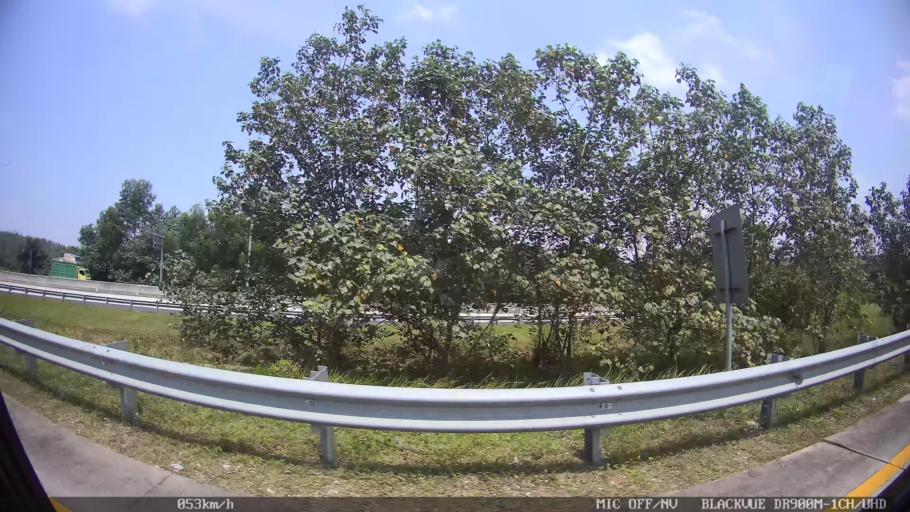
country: ID
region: Lampung
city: Kedaton
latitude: -5.3668
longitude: 105.3266
